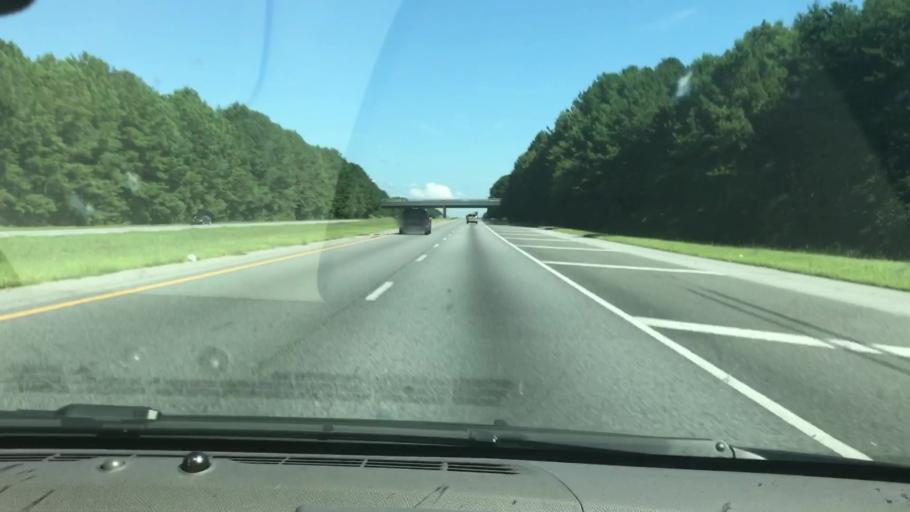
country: US
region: Alabama
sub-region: Russell County
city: Phenix City
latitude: 32.5630
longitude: -84.9622
